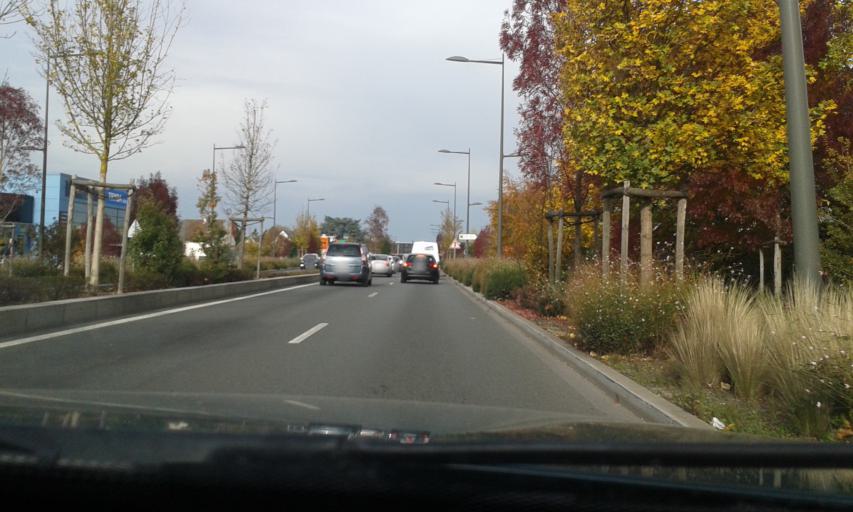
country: FR
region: Centre
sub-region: Departement du Loiret
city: Orleans
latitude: 47.8845
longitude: 1.8981
